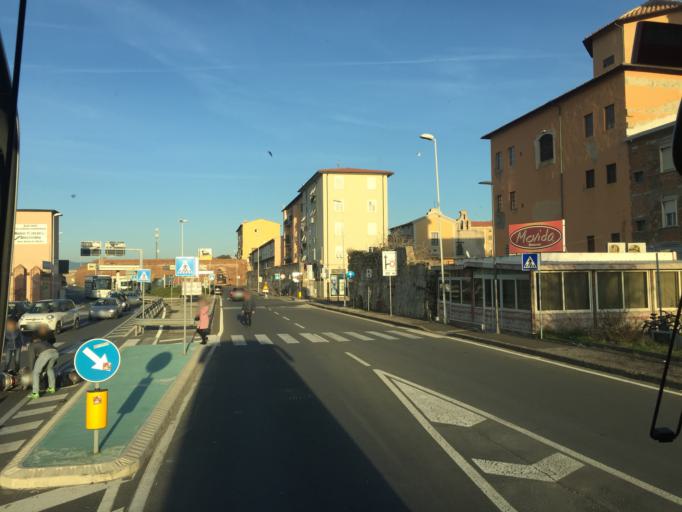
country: IT
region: Tuscany
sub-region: Provincia di Livorno
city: Livorno
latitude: 43.5542
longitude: 10.3042
